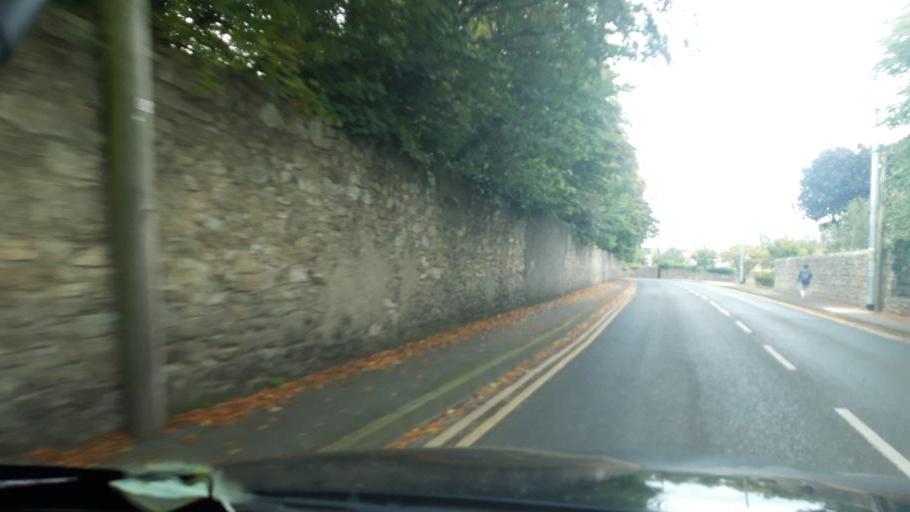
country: IE
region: Leinster
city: Cabinteely
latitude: 53.2628
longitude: -6.1545
